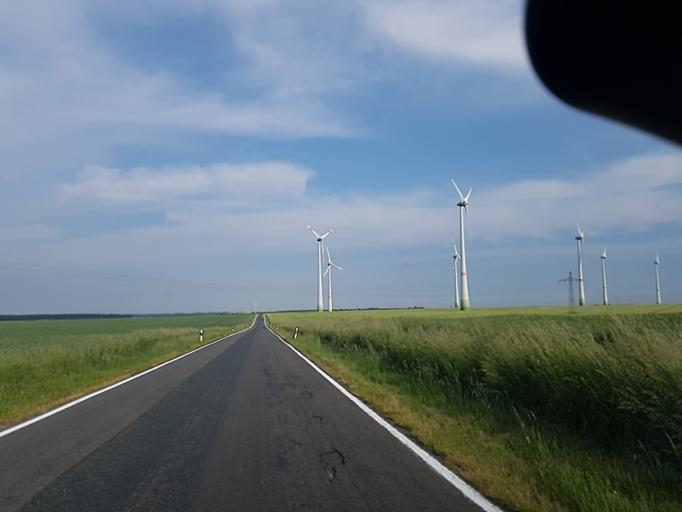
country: DE
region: Saxony-Anhalt
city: Kropstadt
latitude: 51.9810
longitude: 12.8156
